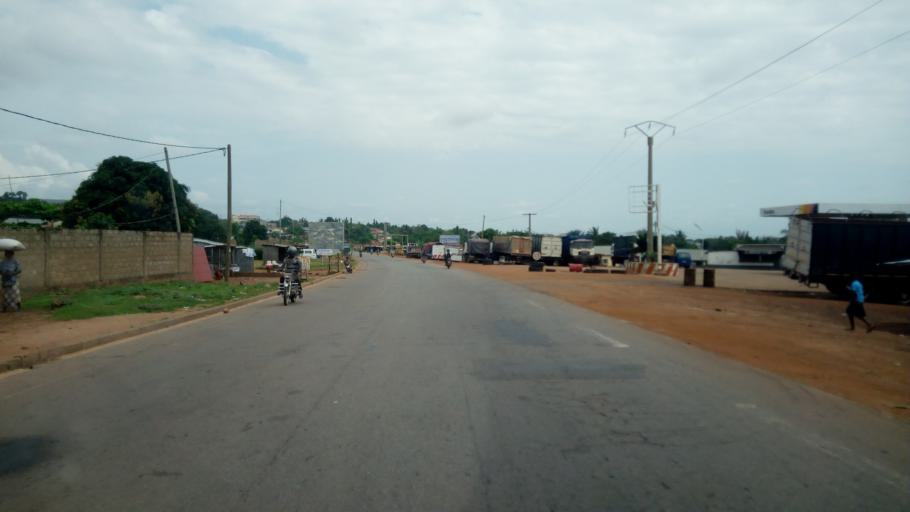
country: TG
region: Plateaux
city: Atakpame
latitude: 7.5018
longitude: 1.1554
